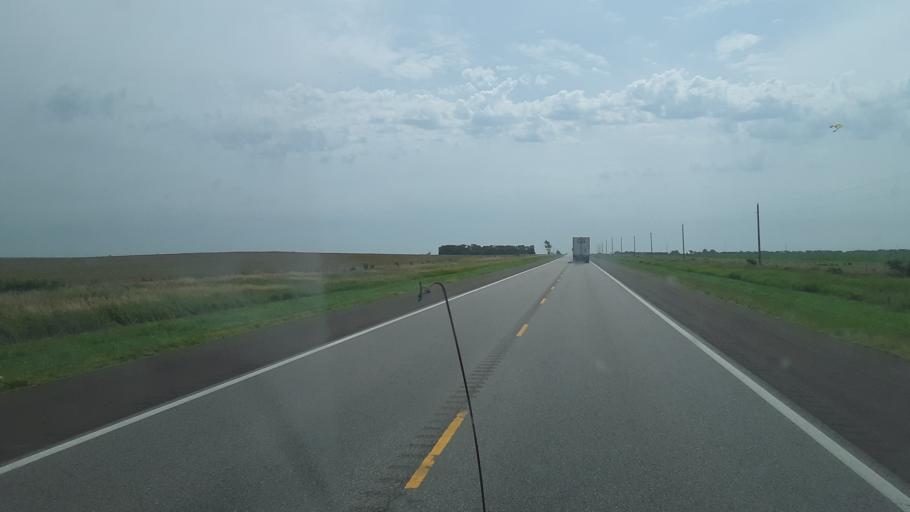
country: US
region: Kansas
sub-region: Reno County
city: Nickerson
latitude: 37.9848
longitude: -98.1332
